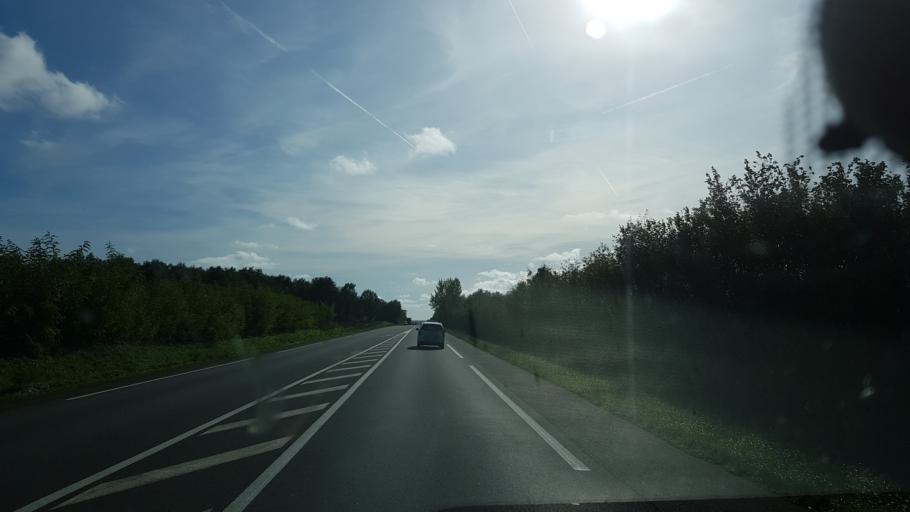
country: FR
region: Poitou-Charentes
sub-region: Departement de la Charente
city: Chasseneuil-sur-Bonnieure
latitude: 45.8547
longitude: 0.4639
